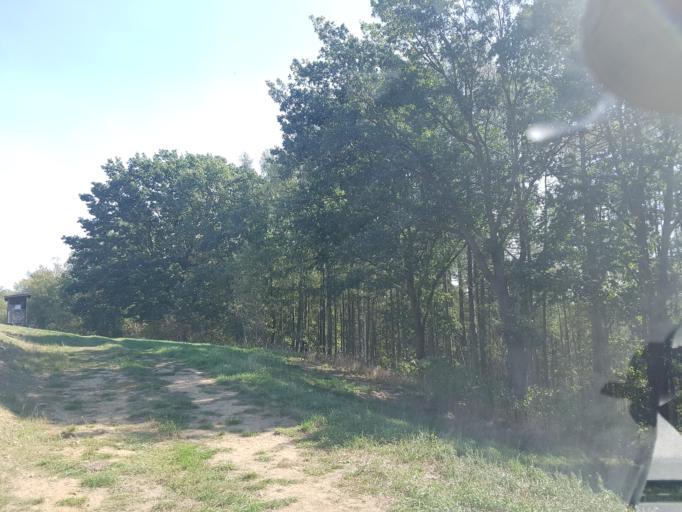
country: DE
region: Saxony
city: Kriebstein
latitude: 51.0514
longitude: 13.0037
